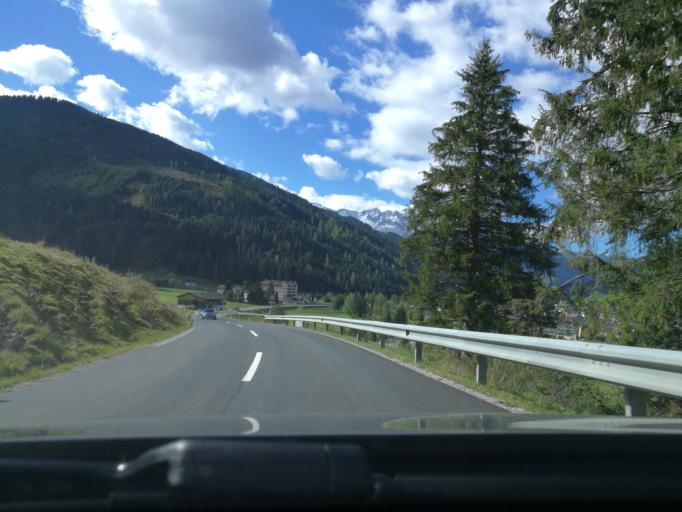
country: AT
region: Tyrol
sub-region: Politischer Bezirk Schwaz
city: Gerlos
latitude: 47.2330
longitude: 12.0547
